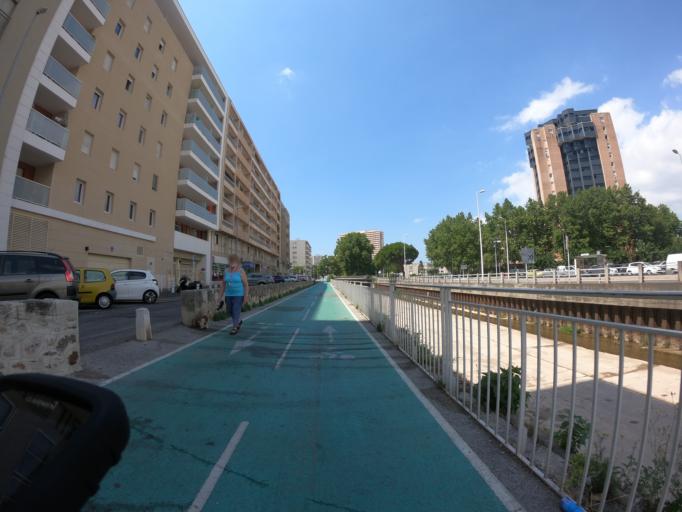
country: FR
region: Provence-Alpes-Cote d'Azur
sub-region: Departement du Var
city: Toulon
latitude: 43.1191
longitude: 5.9470
